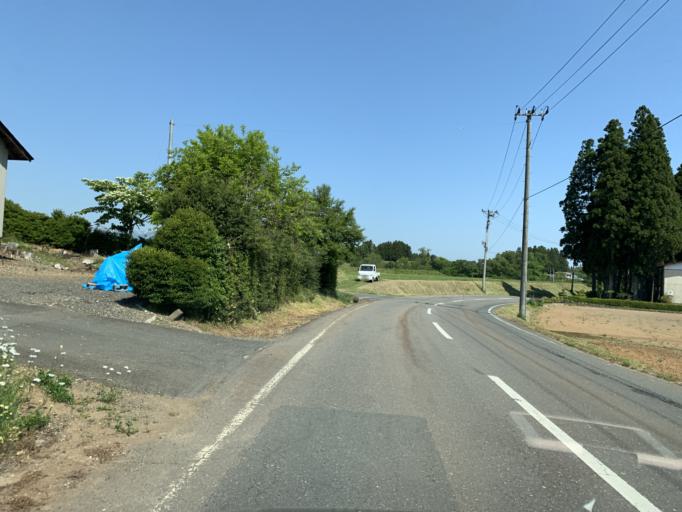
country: JP
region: Iwate
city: Mizusawa
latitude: 39.0748
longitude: 141.0620
